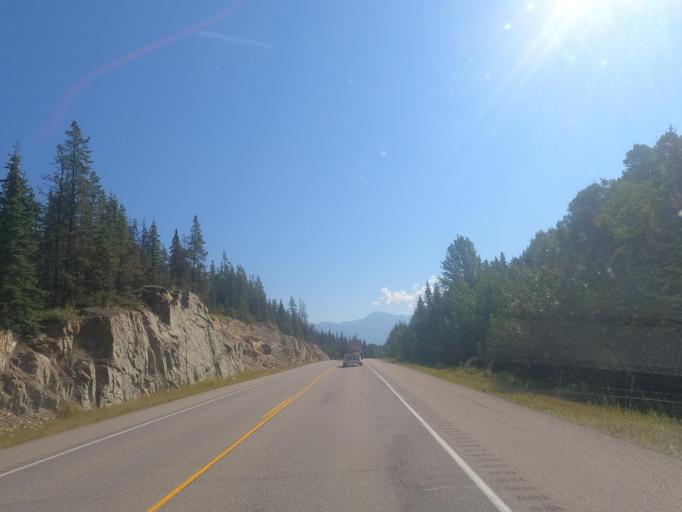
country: CA
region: Alberta
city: Jasper Park Lodge
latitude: 52.8605
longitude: -118.1822
